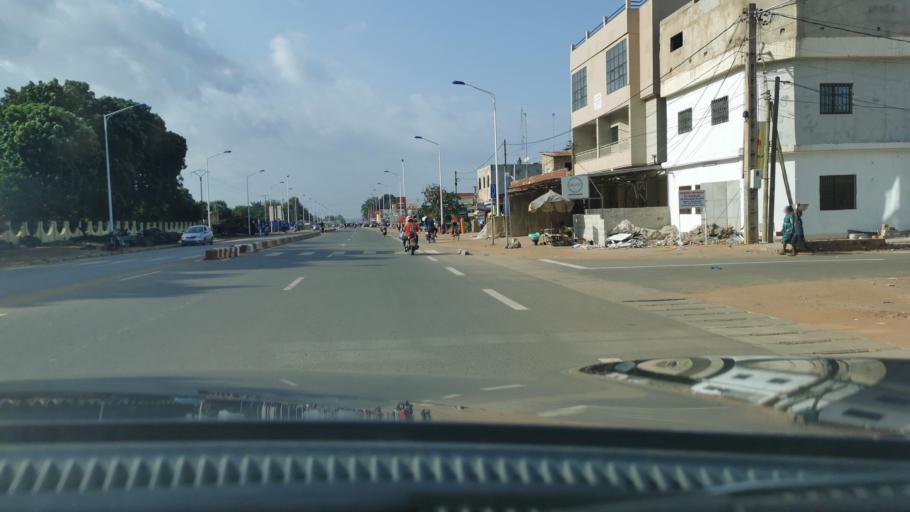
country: TG
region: Maritime
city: Lome
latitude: 6.2018
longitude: 1.2411
